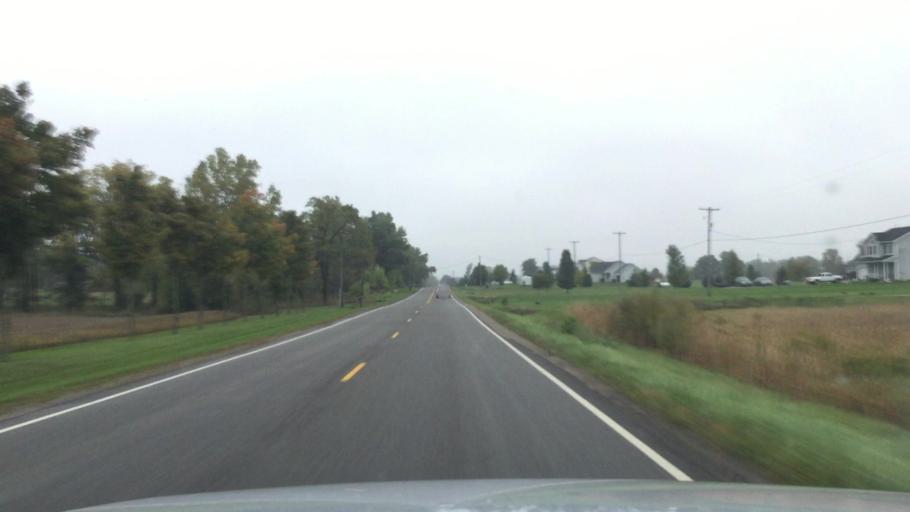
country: US
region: Michigan
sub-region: Shiawassee County
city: Corunna
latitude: 42.9114
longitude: -84.1239
